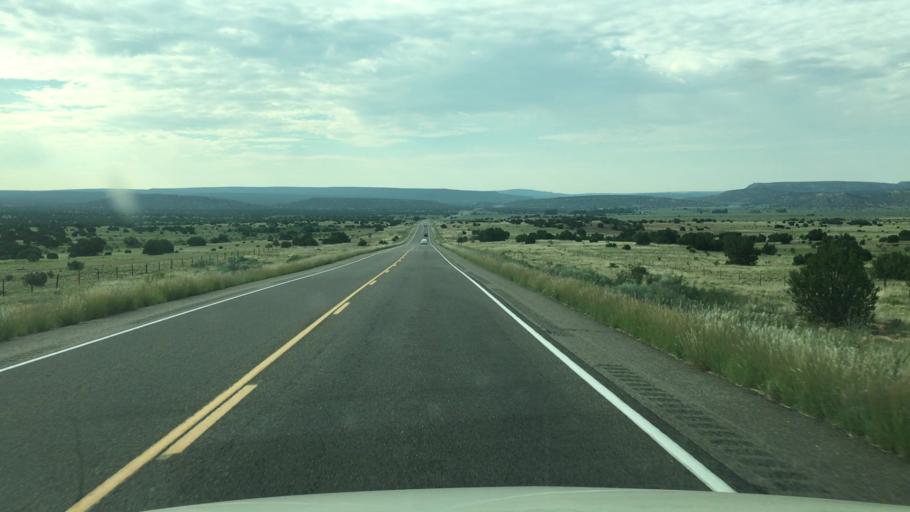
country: US
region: New Mexico
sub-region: Santa Fe County
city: Eldorado at Santa Fe
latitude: 35.4250
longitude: -105.8759
